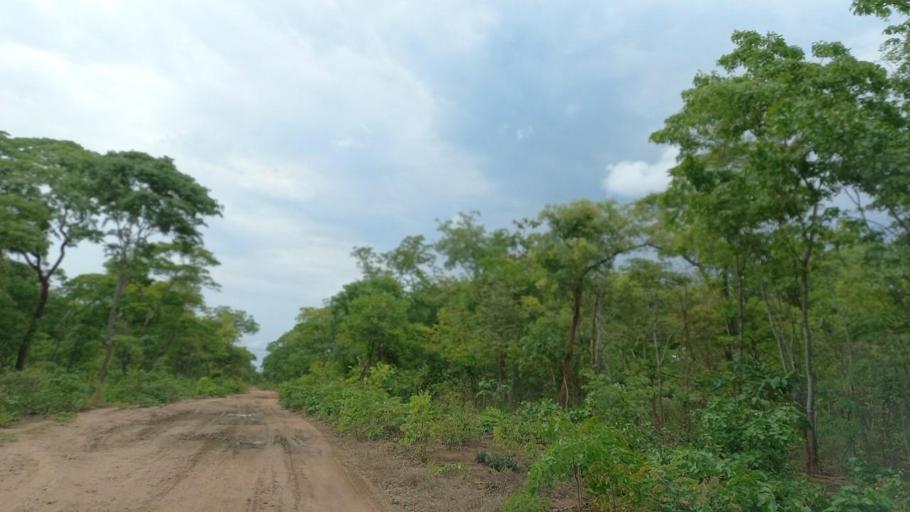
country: ZM
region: North-Western
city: Kalengwa
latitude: -13.5440
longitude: 24.9768
